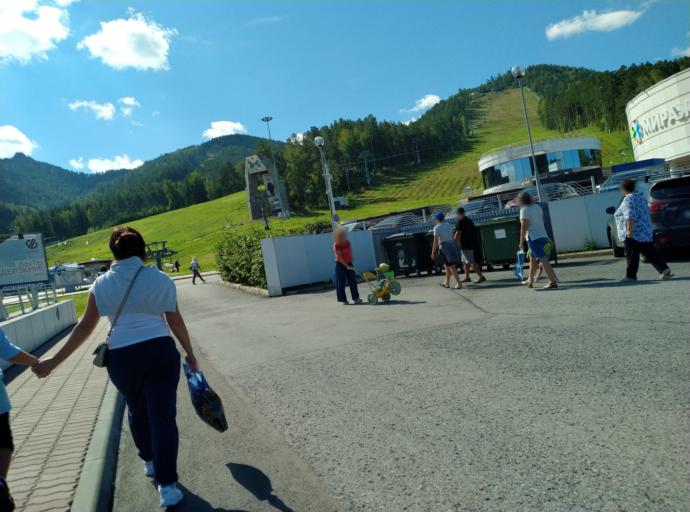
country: RU
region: Krasnoyarskiy
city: Krasnoyarsk
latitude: 55.9627
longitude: 92.7939
